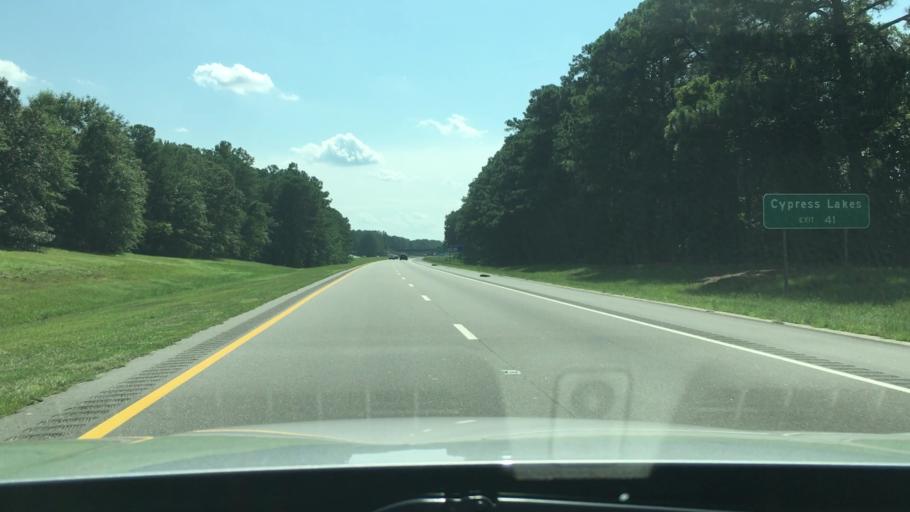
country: US
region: North Carolina
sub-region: Cumberland County
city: Hope Mills
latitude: 34.9427
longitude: -78.9137
